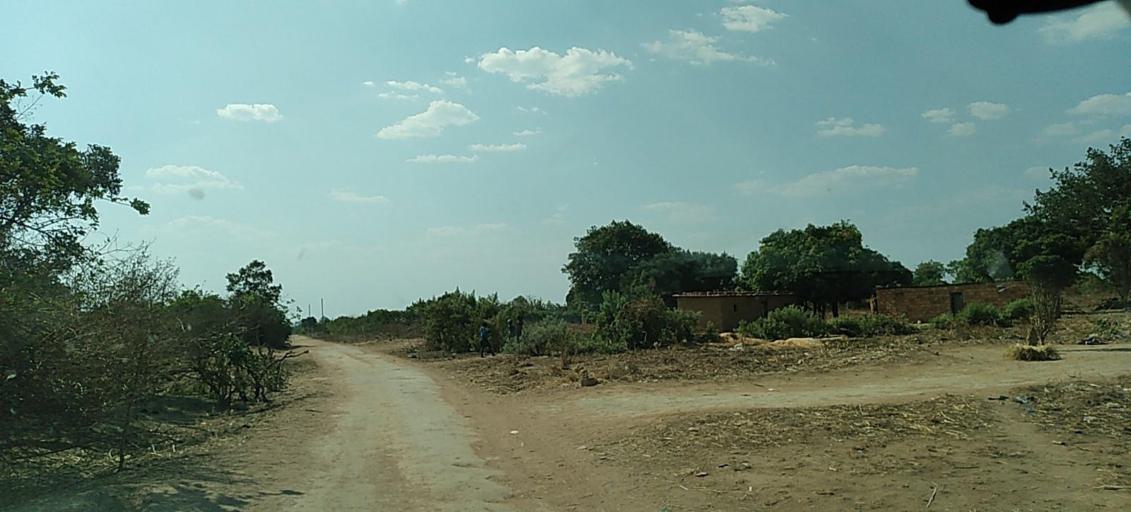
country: ZM
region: North-Western
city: Kalengwa
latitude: -13.1274
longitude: 25.0096
